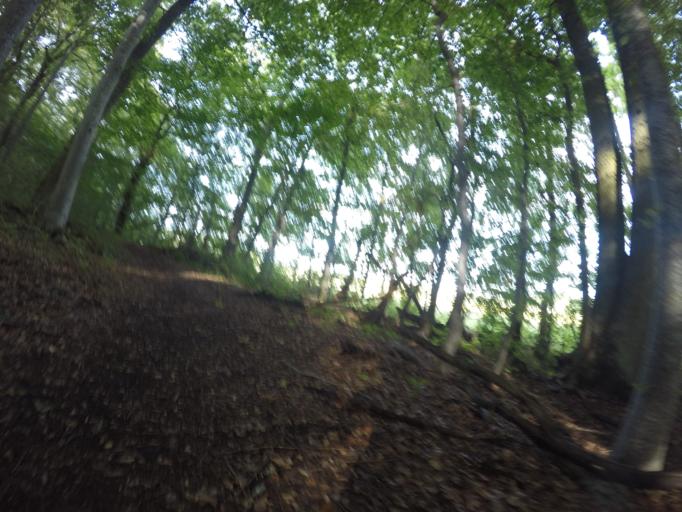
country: SE
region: Soedermanland
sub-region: Eskilstuna Kommun
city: Kvicksund
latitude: 59.4796
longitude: 16.2945
